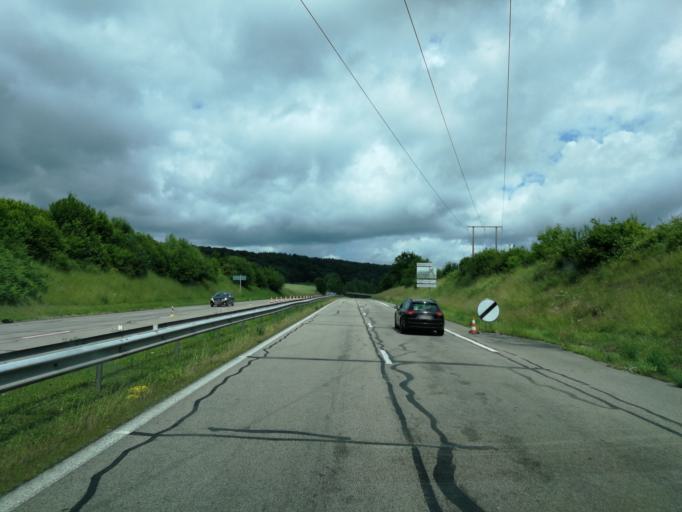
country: FR
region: Haute-Normandie
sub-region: Departement de l'Eure
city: Acquigny
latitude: 49.1670
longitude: 1.1739
